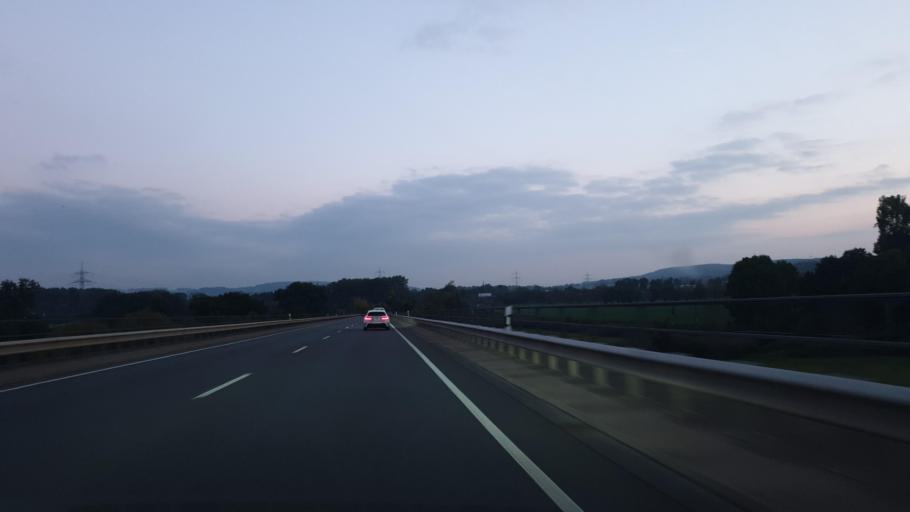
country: DE
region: North Rhine-Westphalia
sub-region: Regierungsbezirk Detmold
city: Kirchlengern
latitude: 52.1950
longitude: 8.6589
